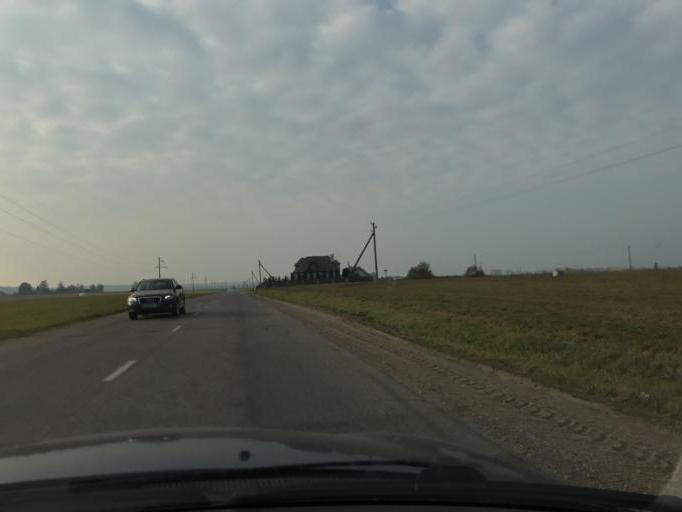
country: BY
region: Grodnenskaya
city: Lida
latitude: 53.8568
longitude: 25.3151
